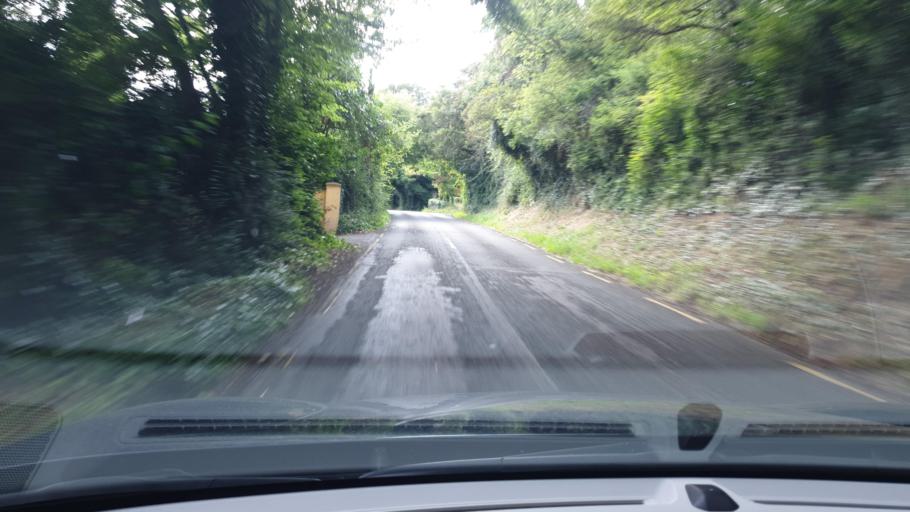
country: IE
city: Palmerstown
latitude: 53.3628
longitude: -6.3759
